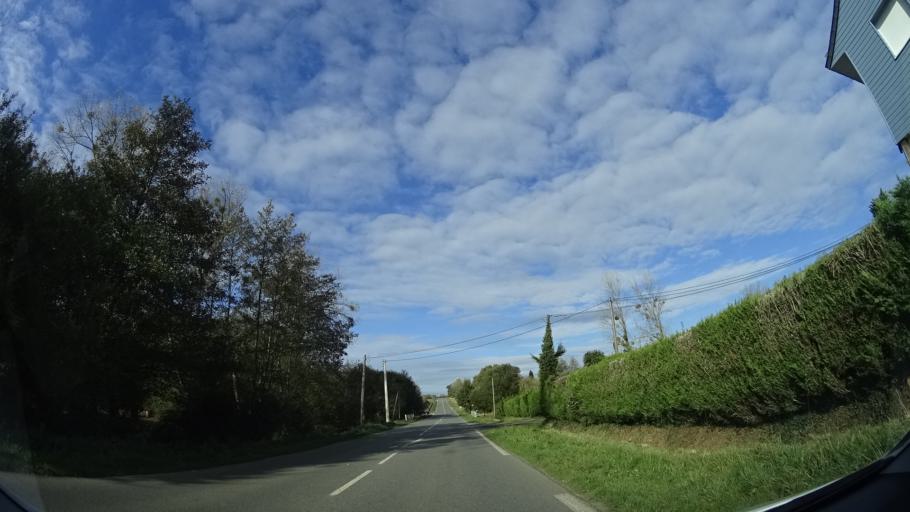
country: FR
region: Brittany
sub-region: Departement d'Ille-et-Vilaine
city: Vignoc
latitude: 48.2456
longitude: -1.8197
